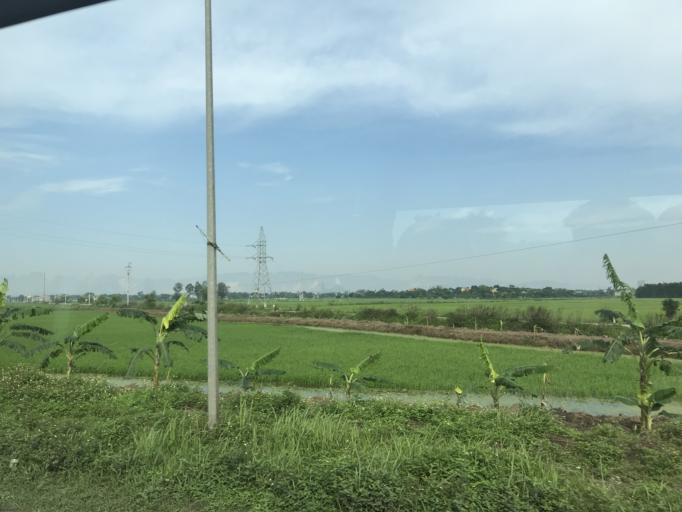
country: VN
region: Ha Nam
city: Thanh Pho Phu Ly
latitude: 20.5153
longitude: 105.9418
